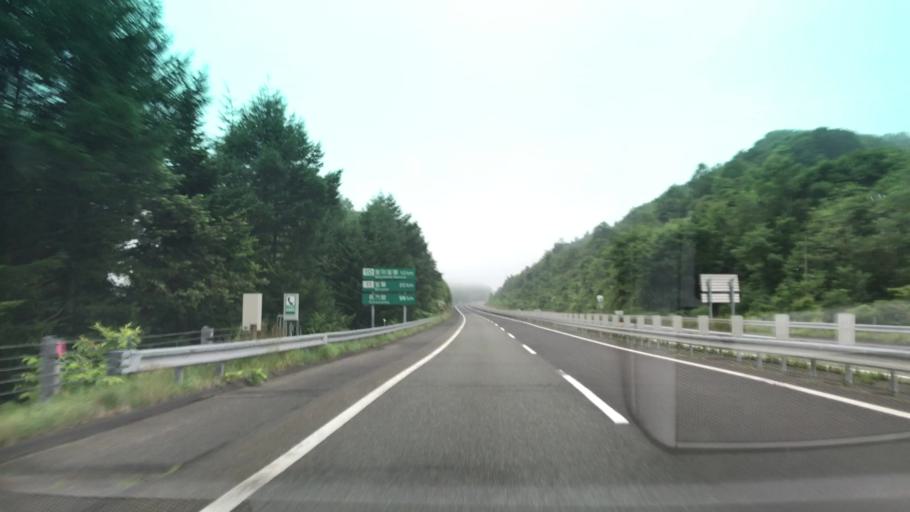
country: JP
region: Hokkaido
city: Shiraoi
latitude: 42.4558
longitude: 141.1653
